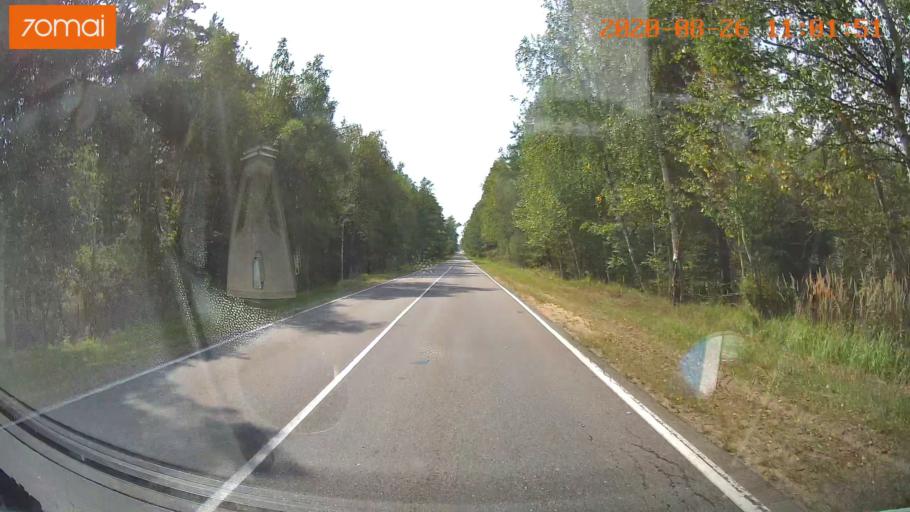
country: RU
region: Rjazan
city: Izhevskoye
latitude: 54.5585
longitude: 41.2274
